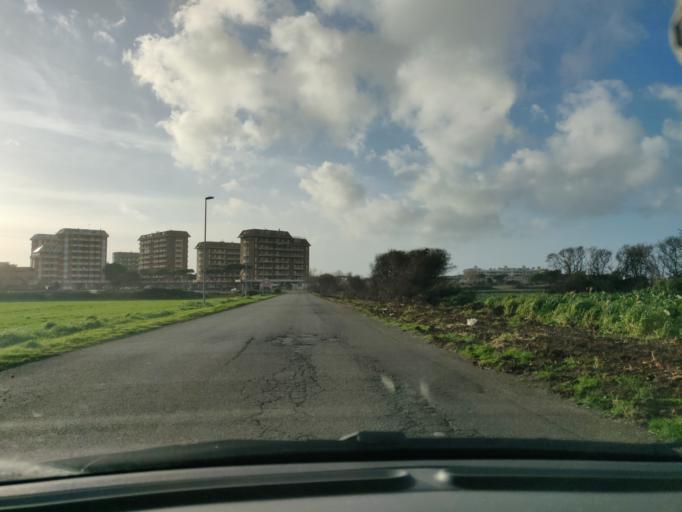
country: IT
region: Latium
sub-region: Provincia di Viterbo
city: Tarquinia
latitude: 42.2250
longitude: 11.7120
